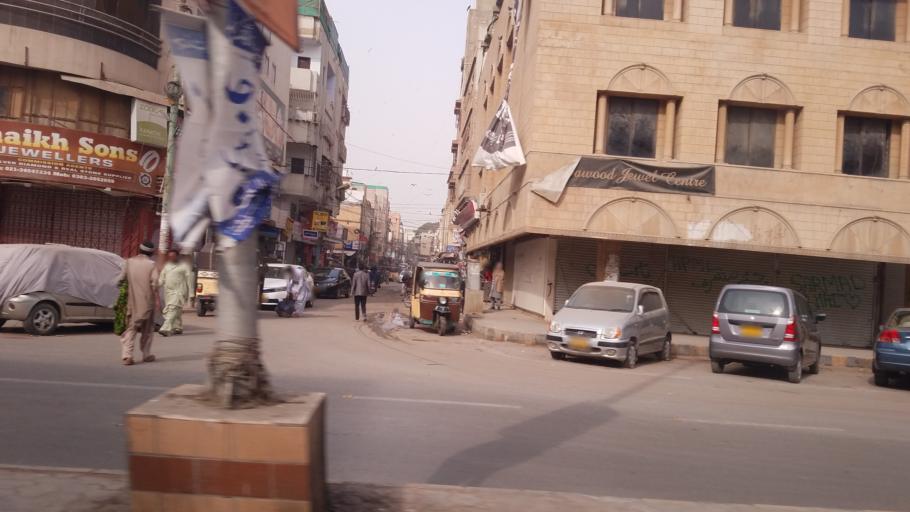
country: PK
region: Sindh
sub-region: Karachi District
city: Karachi
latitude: 24.8710
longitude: 67.0593
